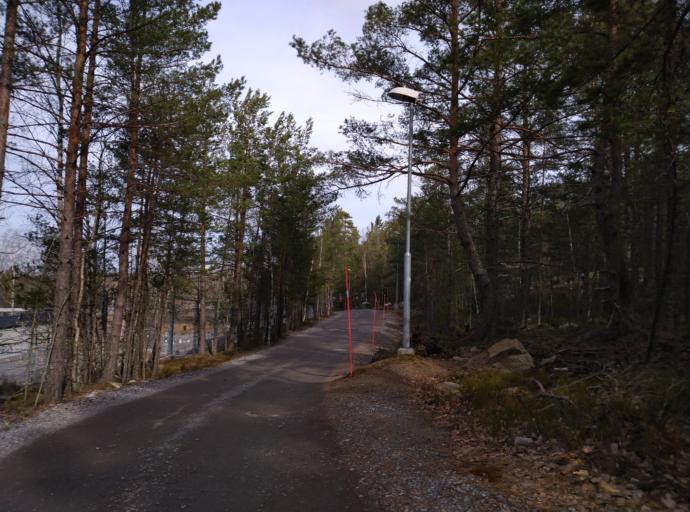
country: SE
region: Stockholm
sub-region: Nacka Kommun
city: Fisksatra
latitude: 59.2910
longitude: 18.2389
